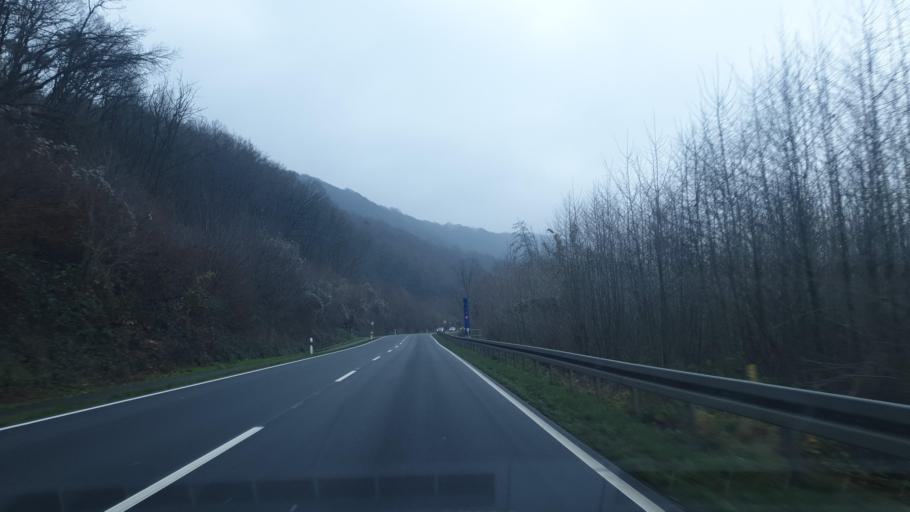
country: DE
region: North Rhine-Westphalia
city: Porta Westfalica
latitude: 52.2450
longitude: 8.8630
